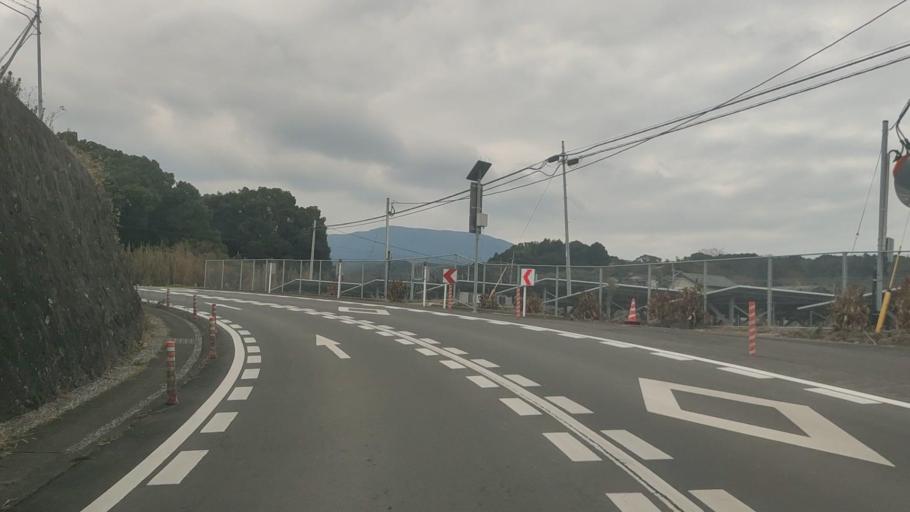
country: JP
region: Nagasaki
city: Shimabara
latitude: 32.8349
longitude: 130.2915
